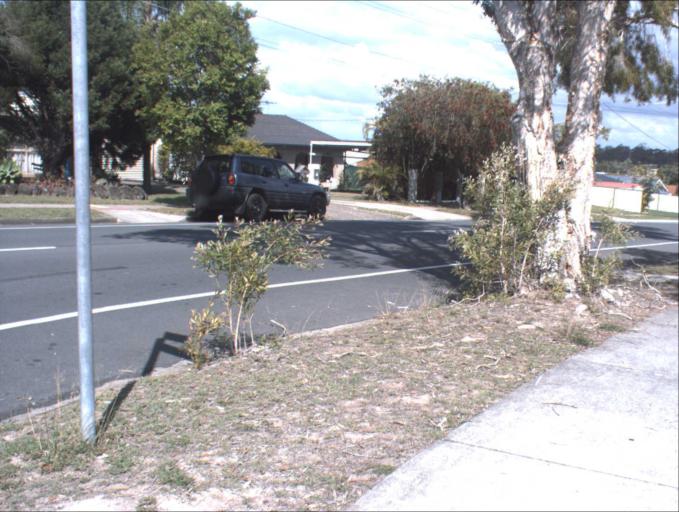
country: AU
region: Queensland
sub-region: Logan
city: Park Ridge South
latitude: -27.6871
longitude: 153.0133
